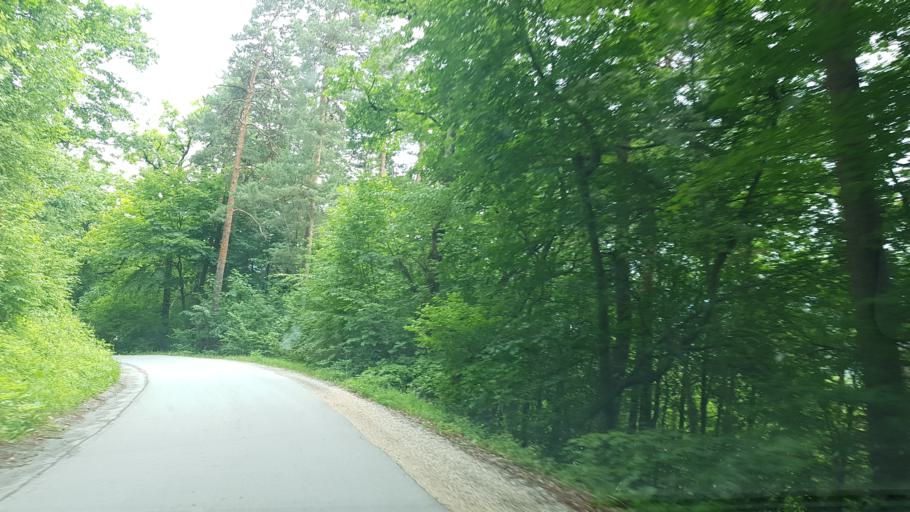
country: SI
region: Dobrna
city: Dobrna
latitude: 46.3504
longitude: 15.2379
